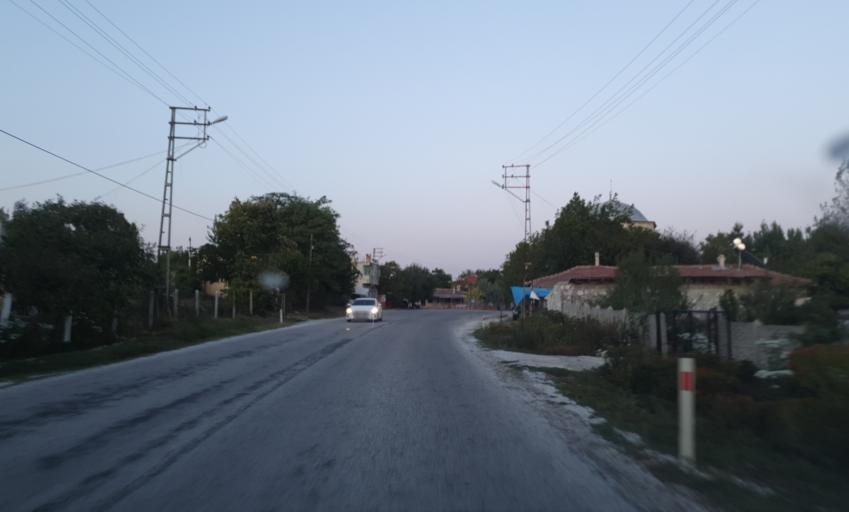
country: TR
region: Kirklareli
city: Pinarhisar
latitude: 41.6272
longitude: 27.5685
